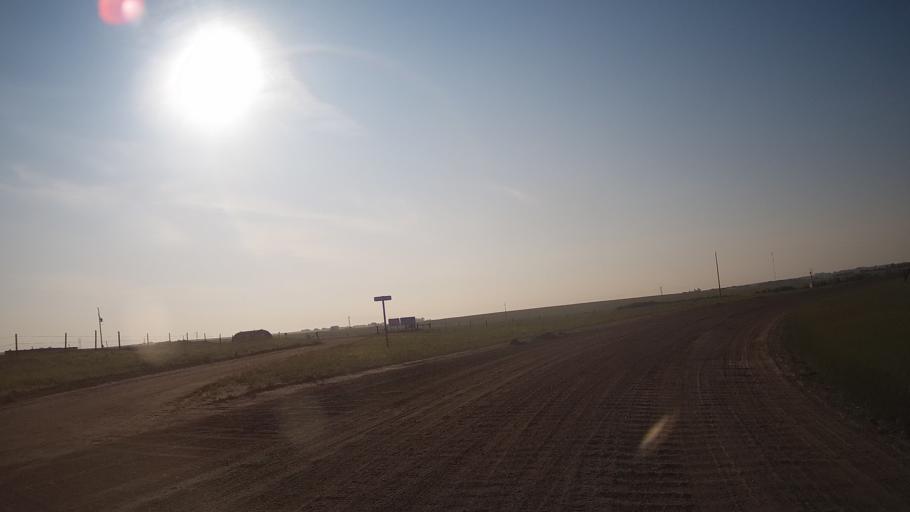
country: CA
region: Saskatchewan
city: Saskatoon
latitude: 51.8236
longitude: -106.5255
